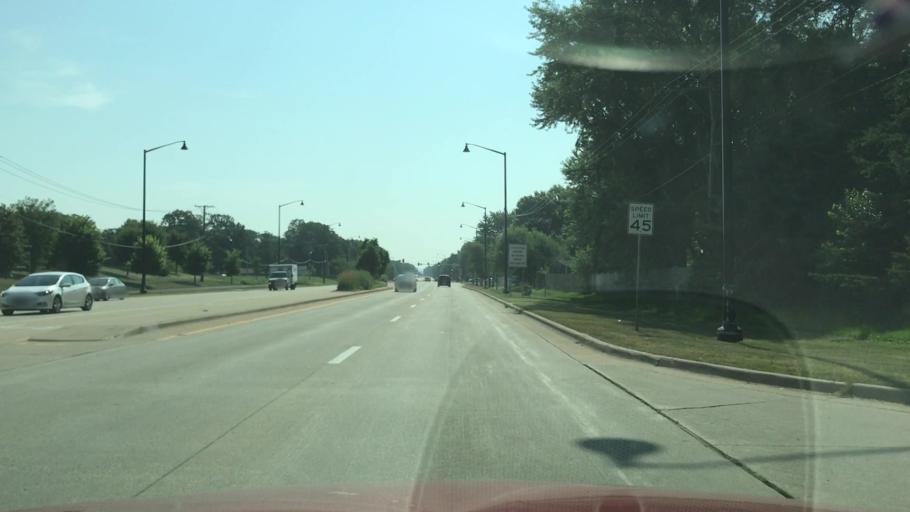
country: US
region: Illinois
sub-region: Winnebago County
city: Cherry Valley
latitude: 42.2384
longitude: -89.0034
